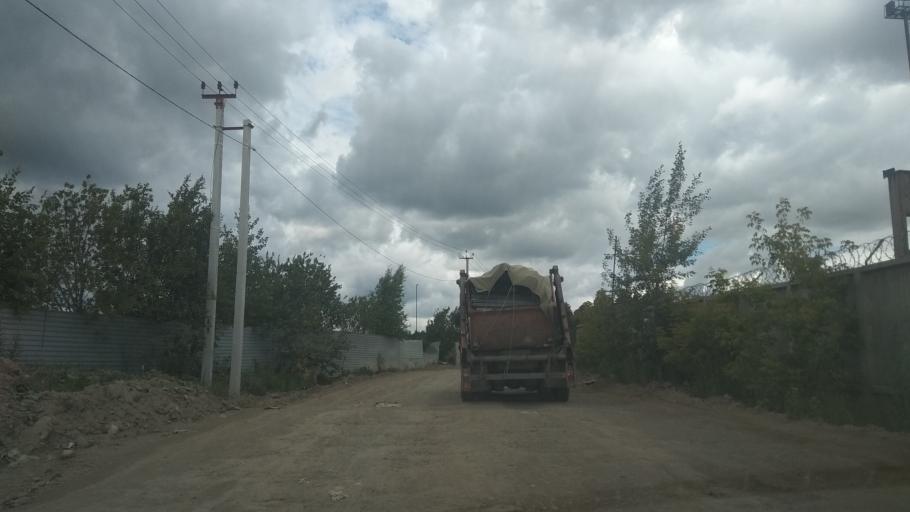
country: RU
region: Sverdlovsk
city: Verkhnyaya Pyshma
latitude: 56.9179
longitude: 60.5718
